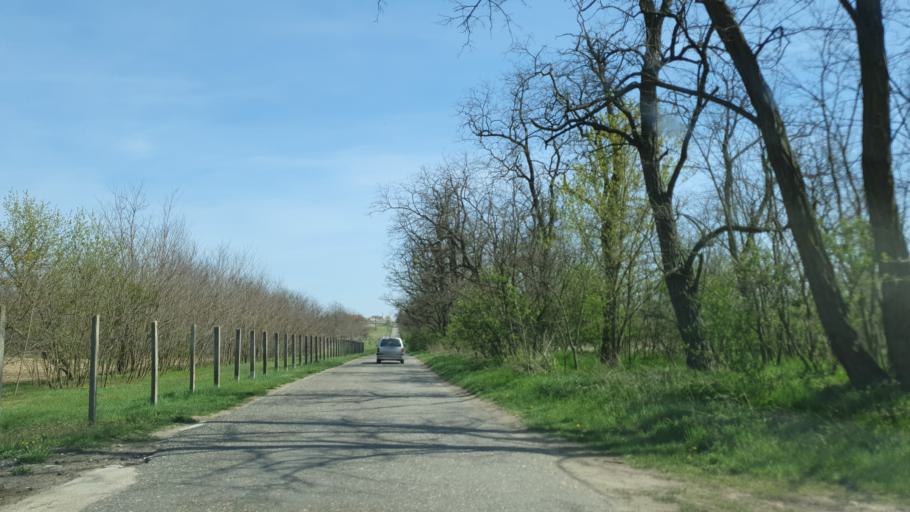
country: HU
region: Komarom-Esztergom
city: Oroszlany
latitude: 47.4947
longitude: 18.2929
